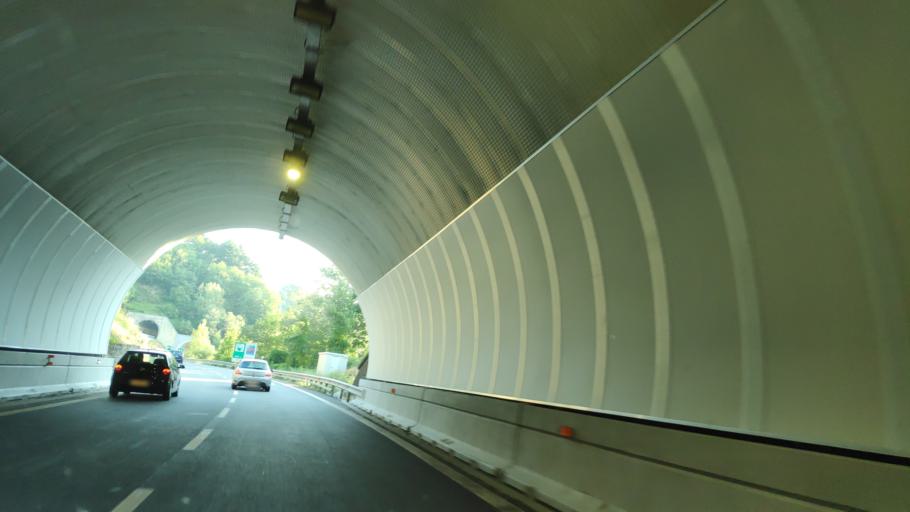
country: IT
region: Calabria
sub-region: Provincia di Cosenza
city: Belsito
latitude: 39.1728
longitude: 16.2938
